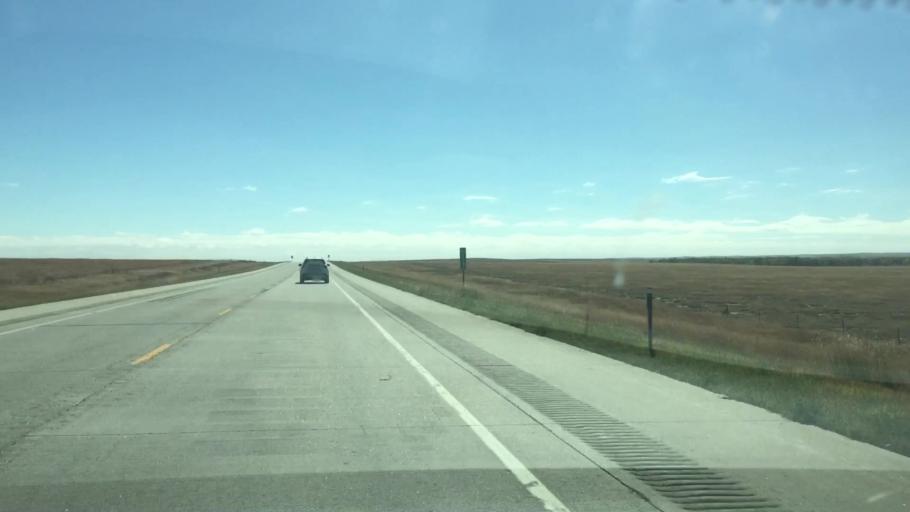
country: US
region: Colorado
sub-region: Lincoln County
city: Hugo
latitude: 39.1896
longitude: -103.5598
